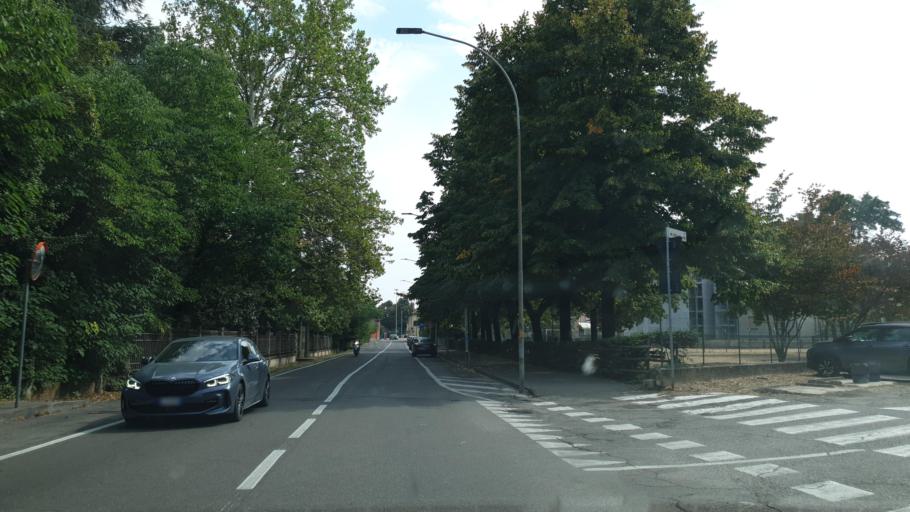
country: IT
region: Emilia-Romagna
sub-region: Provincia di Parma
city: Parma
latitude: 44.8094
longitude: 10.2955
